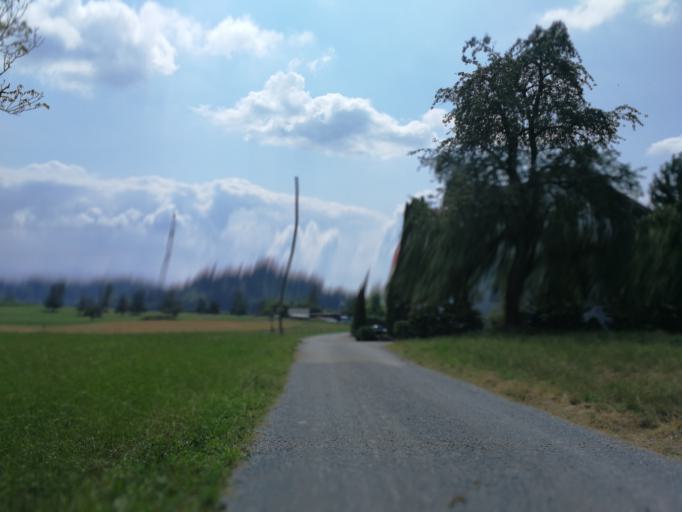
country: CH
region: Zurich
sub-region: Bezirk Hinwil
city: Binzikon
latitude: 47.2774
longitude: 8.7622
